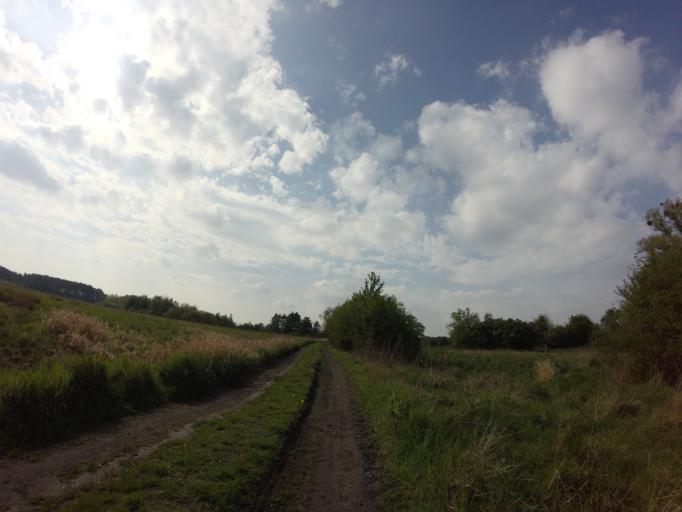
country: PL
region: West Pomeranian Voivodeship
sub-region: Powiat choszczenski
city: Choszczno
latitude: 53.1699
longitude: 15.3920
